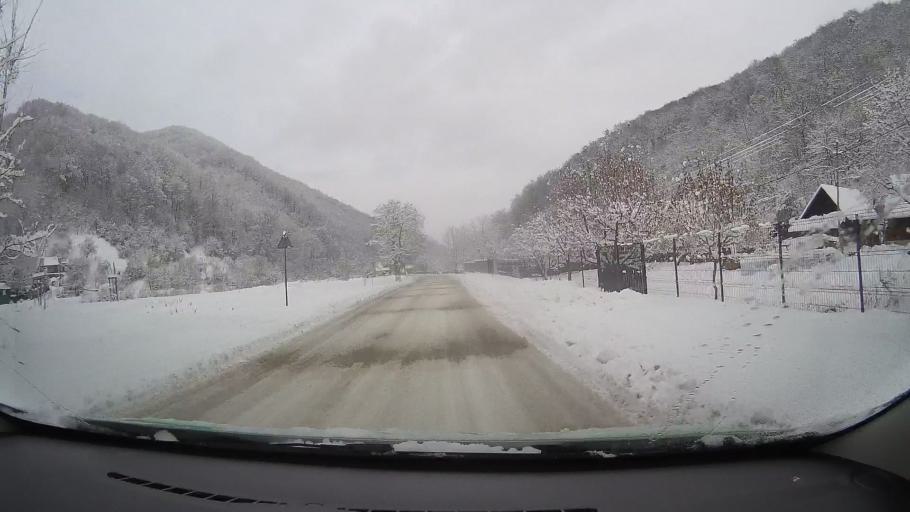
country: RO
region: Alba
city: Pianu de Sus
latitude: 45.8592
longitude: 23.4999
